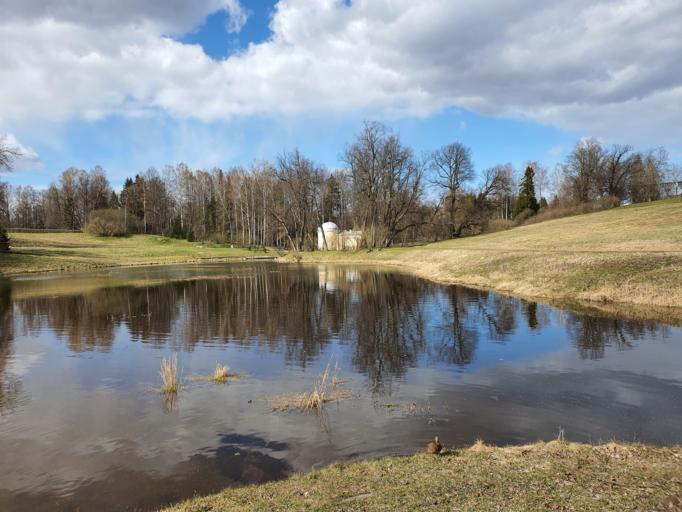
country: RU
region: St.-Petersburg
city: Pavlovsk
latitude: 59.6847
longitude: 30.4503
